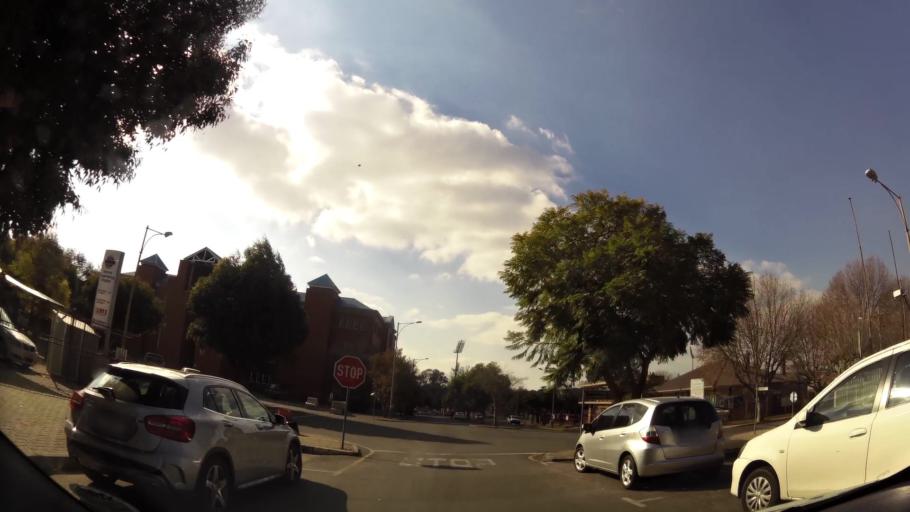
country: ZA
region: Gauteng
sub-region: West Rand District Municipality
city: Krugersdorp
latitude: -26.1045
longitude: 27.7762
